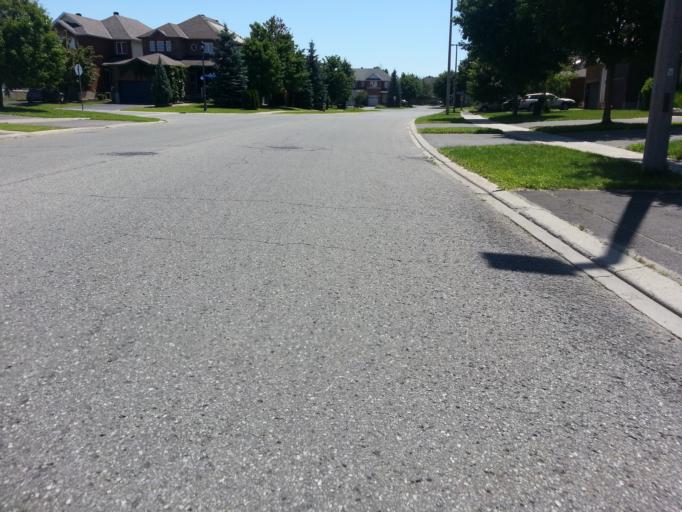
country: CA
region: Ontario
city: Bells Corners
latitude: 45.3187
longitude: -75.9253
